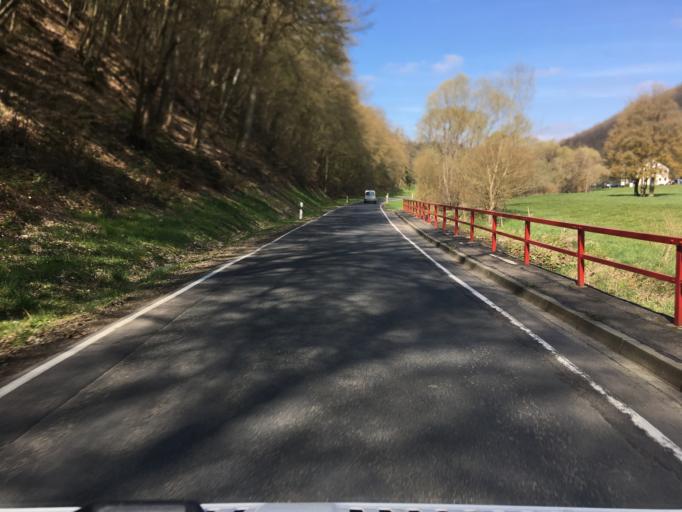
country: DE
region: Rheinland-Pfalz
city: Kirchsahr
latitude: 50.5094
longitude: 6.9130
